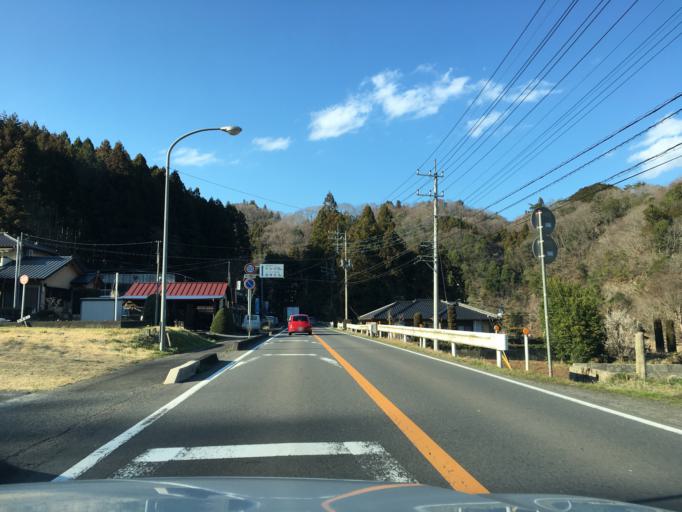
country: JP
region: Ibaraki
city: Daigo
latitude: 36.7342
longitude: 140.3899
